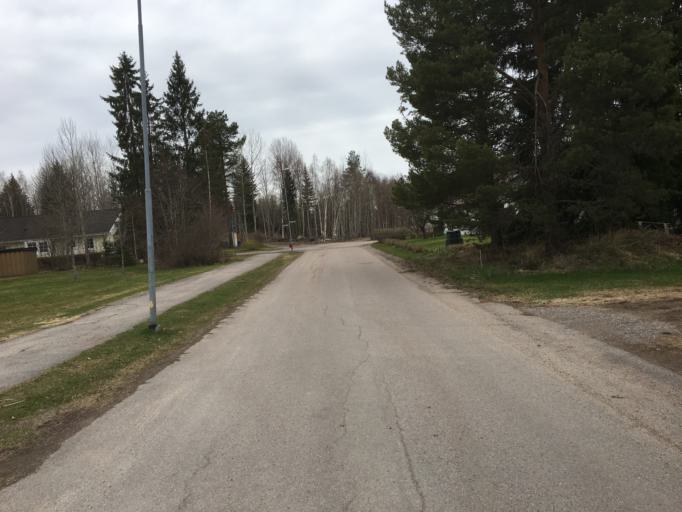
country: SE
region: Gaevleborg
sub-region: Hofors Kommun
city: Hofors
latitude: 60.5144
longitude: 16.4699
